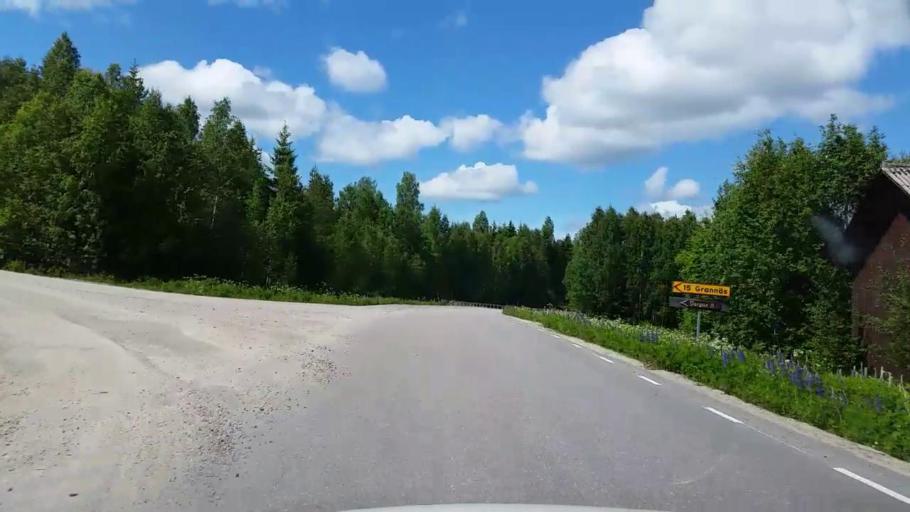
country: SE
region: Gaevleborg
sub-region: Ovanakers Kommun
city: Alfta
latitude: 61.2597
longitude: 16.1233
